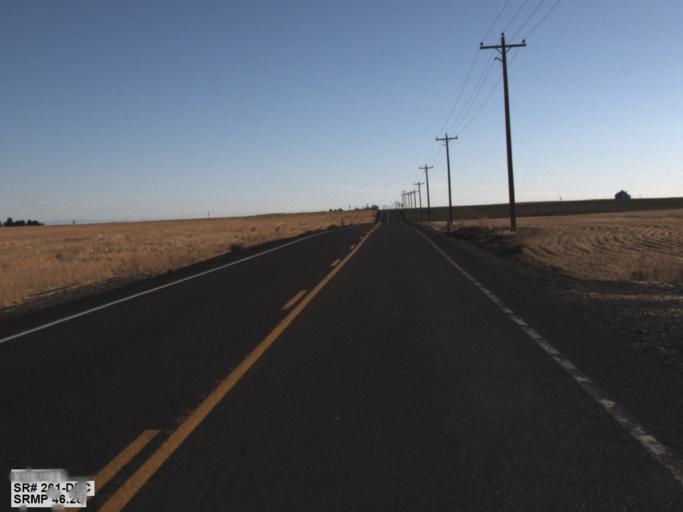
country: US
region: Washington
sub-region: Adams County
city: Ritzville
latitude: 46.8897
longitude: -118.3341
